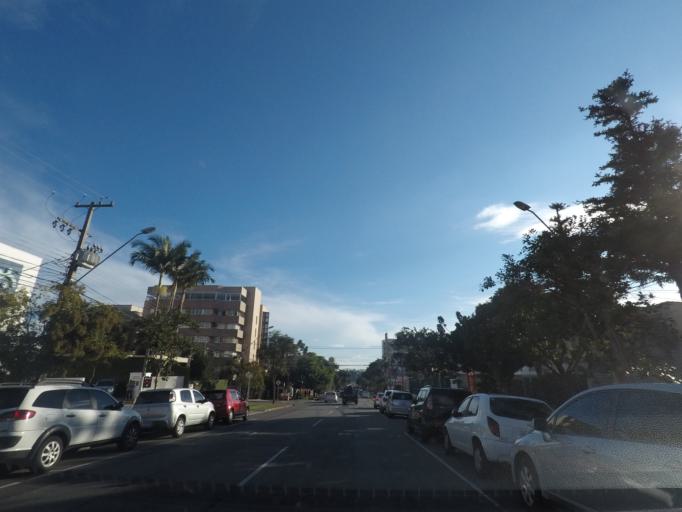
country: BR
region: Parana
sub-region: Curitiba
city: Curitiba
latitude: -25.4482
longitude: -49.2943
